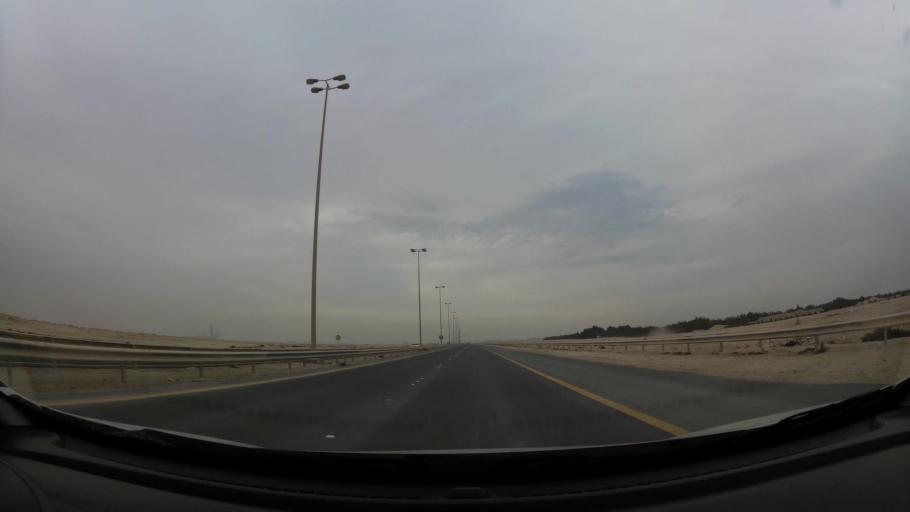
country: BH
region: Central Governorate
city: Dar Kulayb
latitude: 26.0119
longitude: 50.6065
